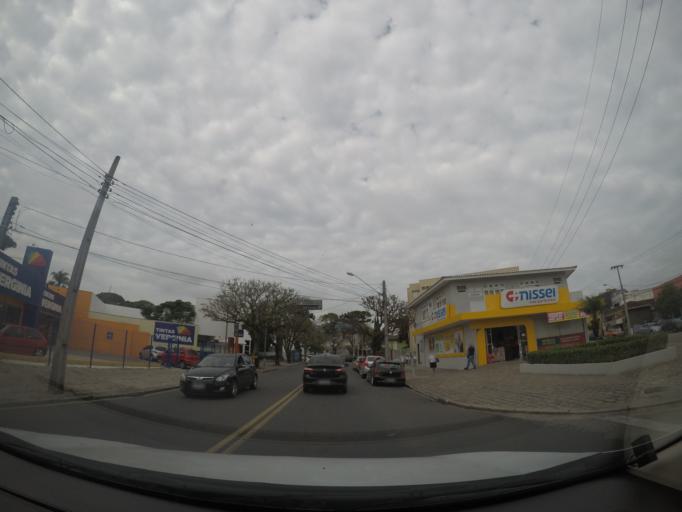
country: BR
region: Parana
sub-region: Curitiba
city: Curitiba
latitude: -25.4134
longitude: -49.2795
